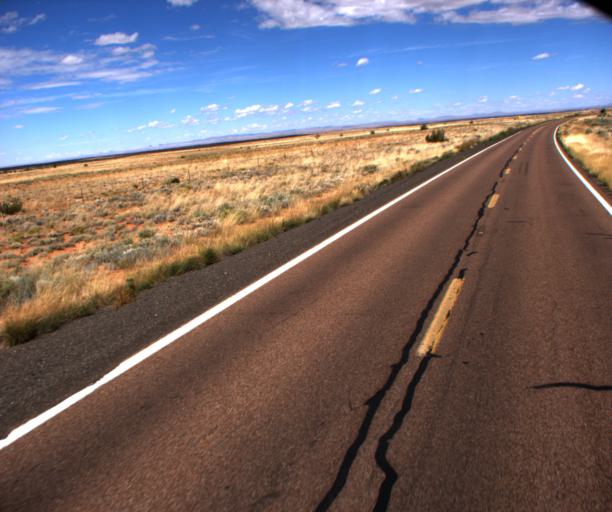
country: US
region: Arizona
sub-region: Navajo County
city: Holbrook
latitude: 34.7192
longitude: -110.2950
